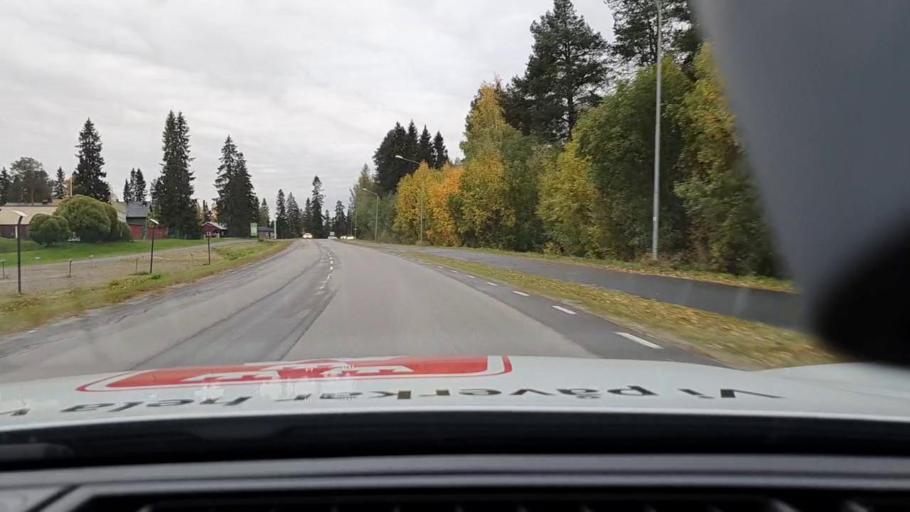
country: SE
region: Norrbotten
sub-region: Bodens Kommun
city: Boden
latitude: 65.8120
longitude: 21.6771
